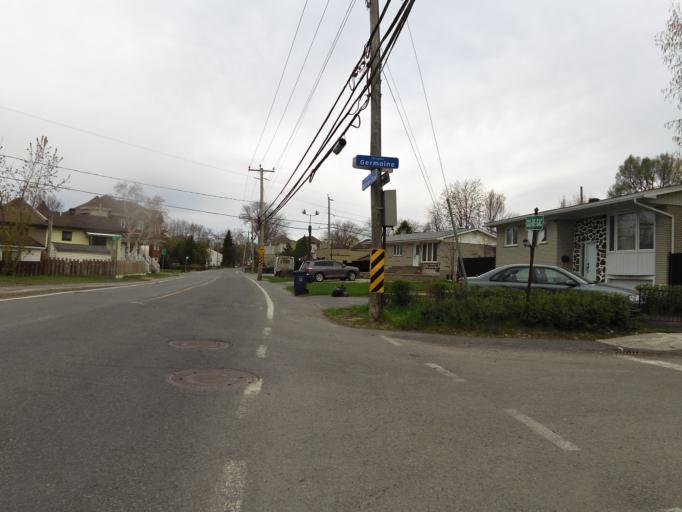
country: CA
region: Quebec
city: Dollard-Des Ormeaux
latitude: 45.5187
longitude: -73.7998
